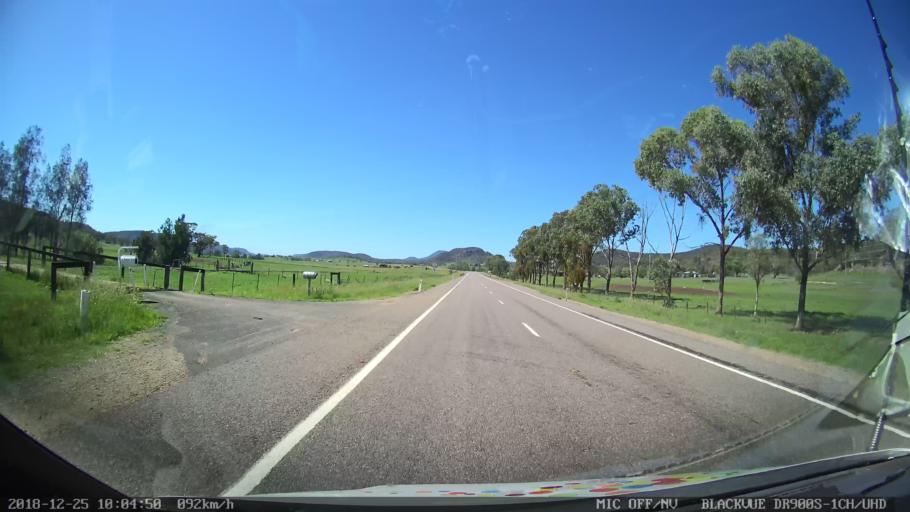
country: AU
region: New South Wales
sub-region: Upper Hunter Shire
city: Merriwa
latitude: -32.2393
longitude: 150.4860
